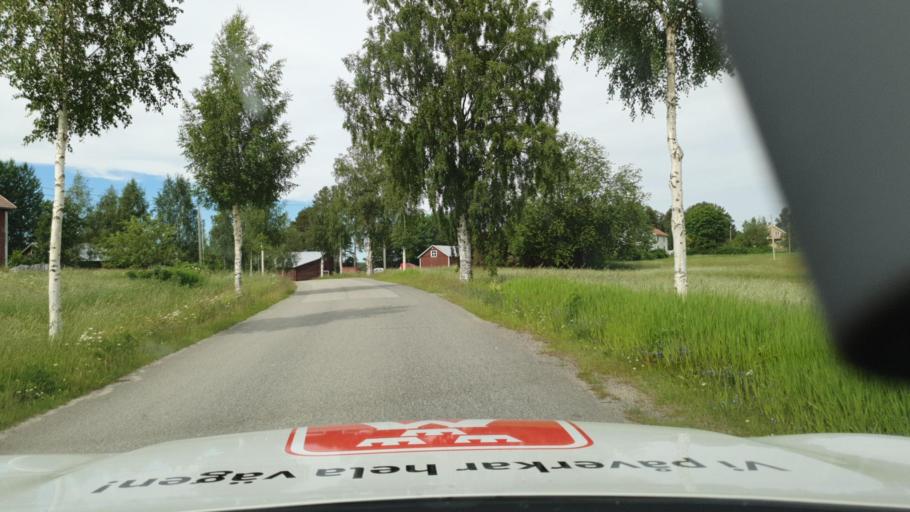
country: SE
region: Vaesterbotten
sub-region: Skelleftea Kommun
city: Burtraesk
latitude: 64.4544
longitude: 20.4798
